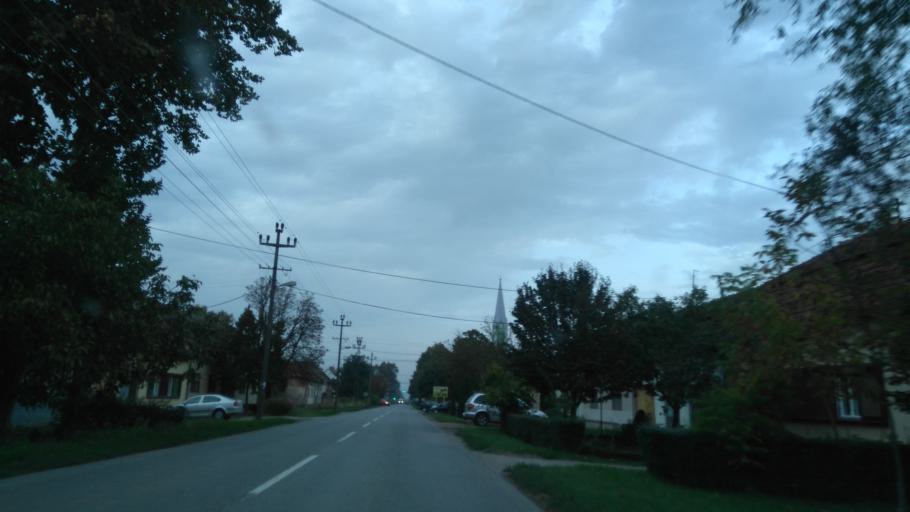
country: RS
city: Mol
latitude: 45.7607
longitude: 20.1301
